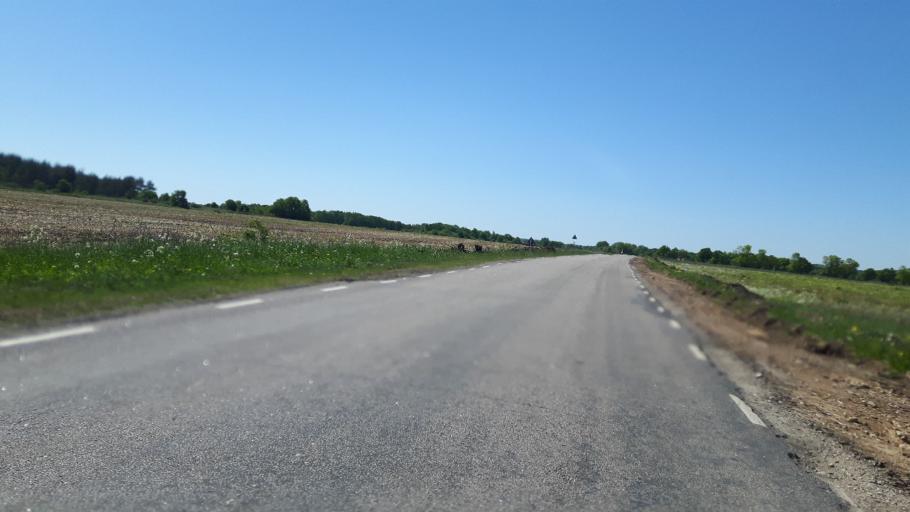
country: EE
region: Ida-Virumaa
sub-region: Narva-Joesuu linn
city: Narva-Joesuu
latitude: 59.4010
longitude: 27.9355
